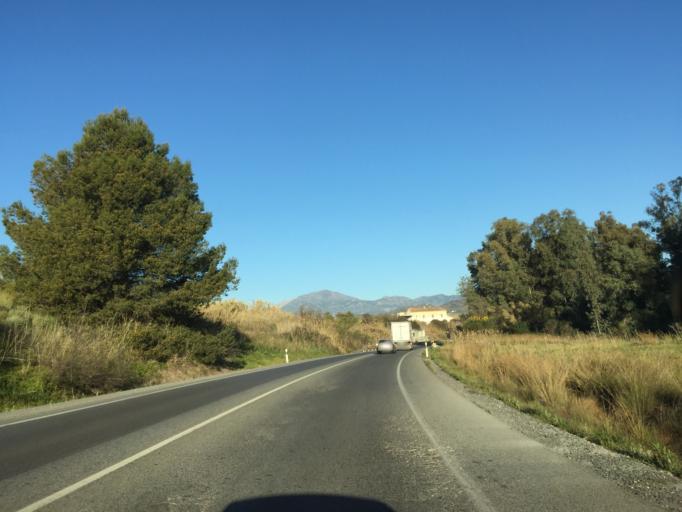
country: ES
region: Andalusia
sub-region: Provincia de Malaga
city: Pizarra
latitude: 36.7200
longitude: -4.7058
